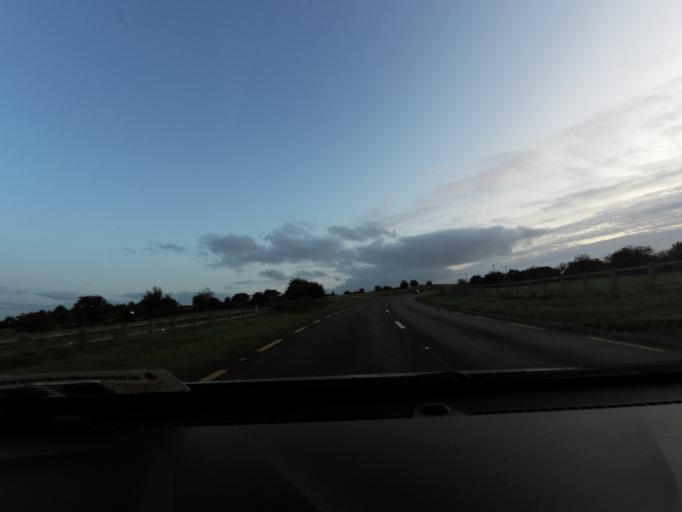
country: IE
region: Connaught
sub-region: County Galway
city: Tuam
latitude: 53.4103
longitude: -8.8067
